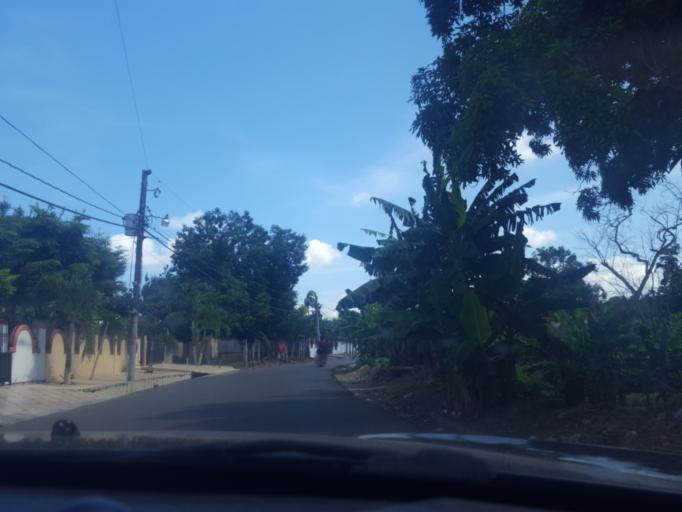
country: DO
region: Santiago
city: Baitoa
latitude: 19.3765
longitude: -70.6517
